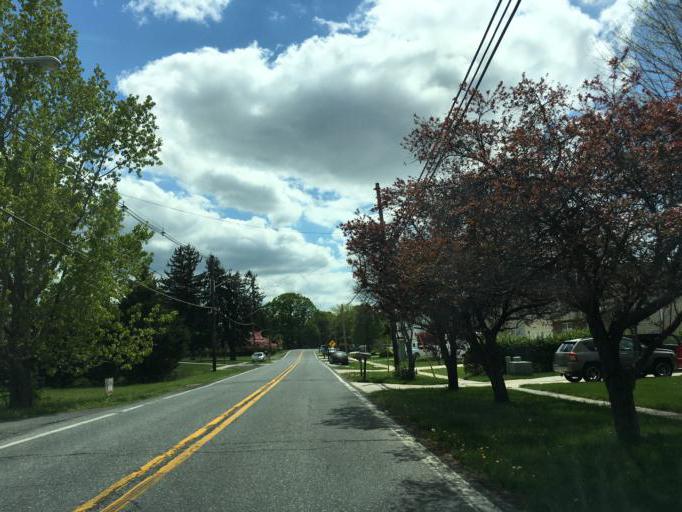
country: US
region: Maryland
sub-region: Frederick County
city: Thurmont
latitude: 39.6312
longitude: -77.4084
